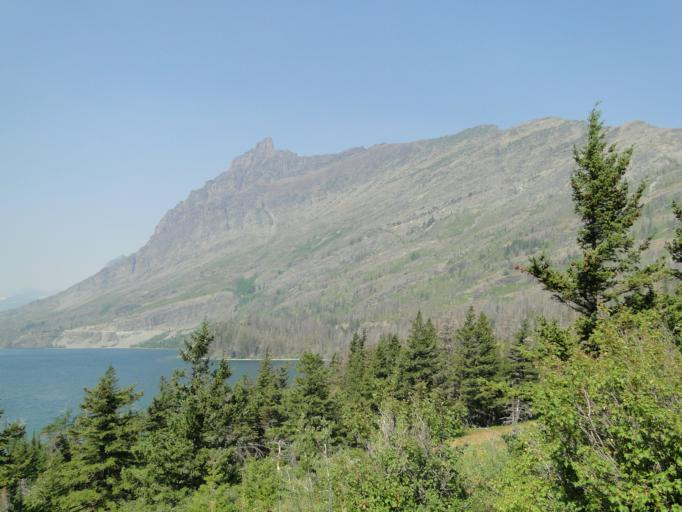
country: US
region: Montana
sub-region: Glacier County
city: Browning
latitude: 48.6917
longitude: -113.5315
